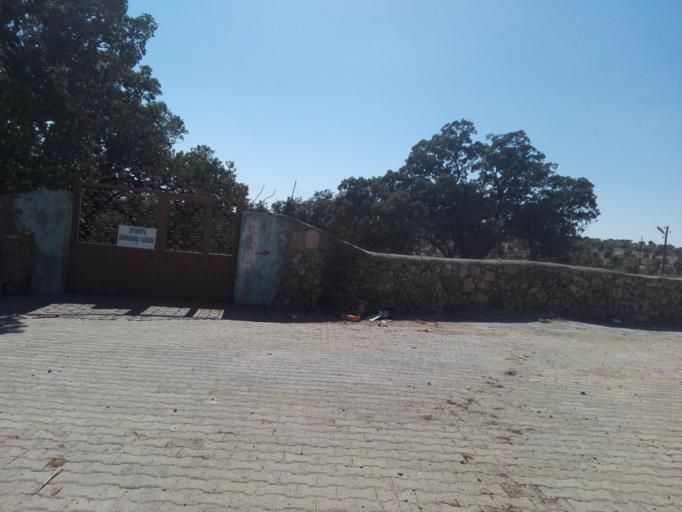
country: TR
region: Mardin
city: Kilavuz
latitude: 37.4788
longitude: 41.7768
